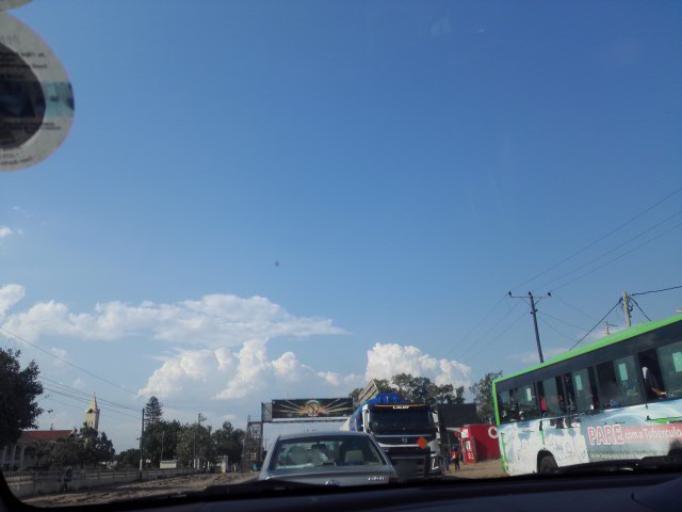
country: MZ
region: Maputo City
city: Maputo
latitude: -25.8605
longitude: 32.5667
